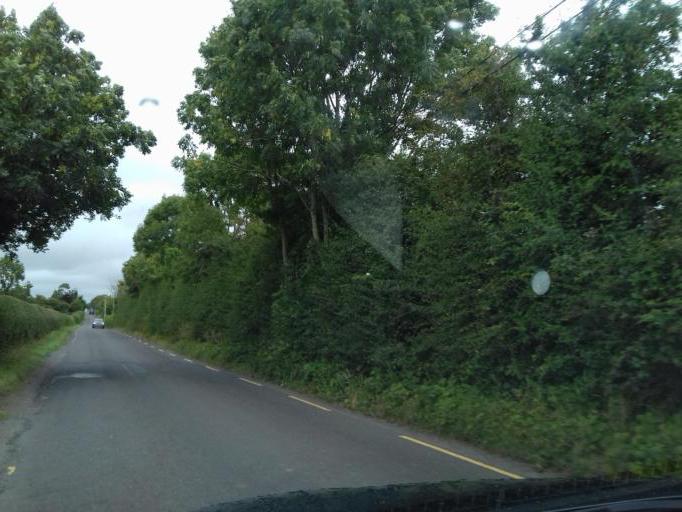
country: IE
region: Leinster
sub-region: Kilkenny
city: Graiguenamanagh
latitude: 52.6151
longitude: -7.0345
